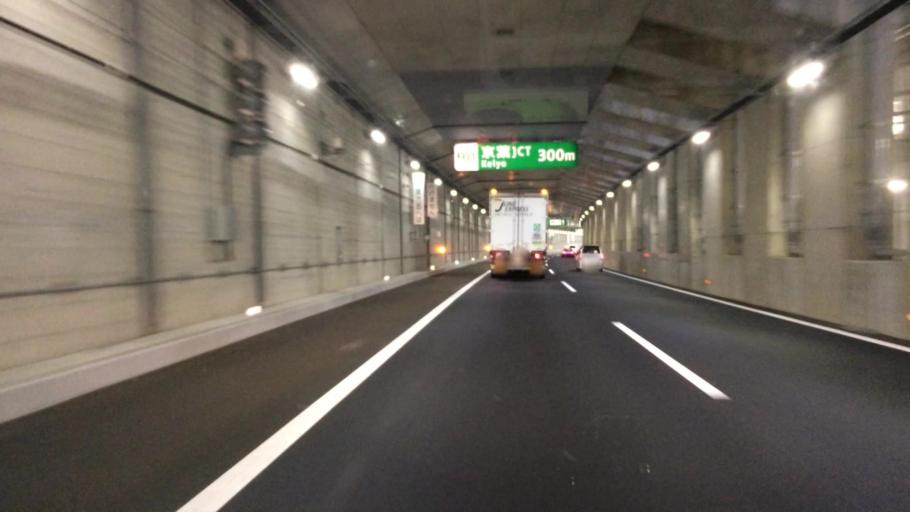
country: JP
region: Chiba
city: Funabashi
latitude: 35.7011
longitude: 139.9323
